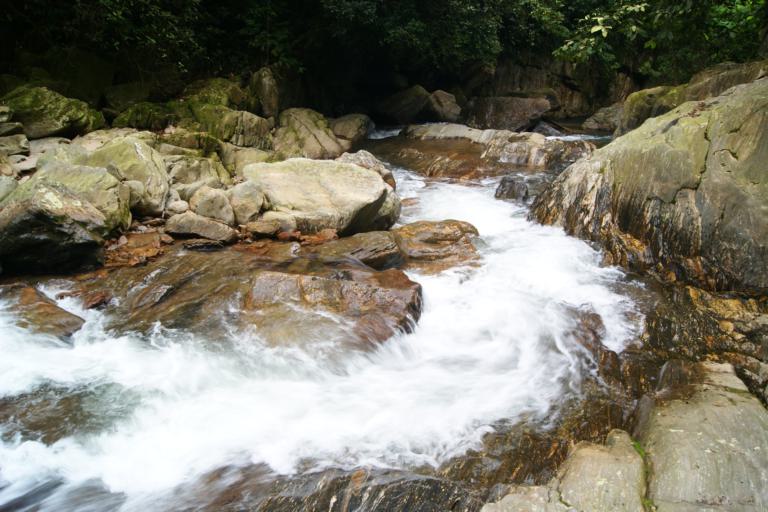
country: BR
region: Sao Paulo
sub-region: Cubatao
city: Cubatao
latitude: -23.8411
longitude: -46.4206
